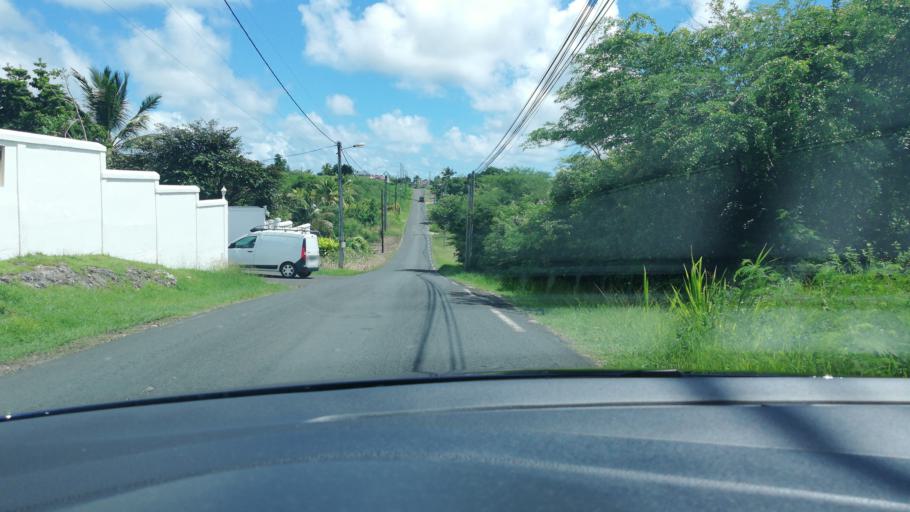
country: GP
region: Guadeloupe
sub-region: Guadeloupe
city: Petit-Canal
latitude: 16.3787
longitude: -61.4470
